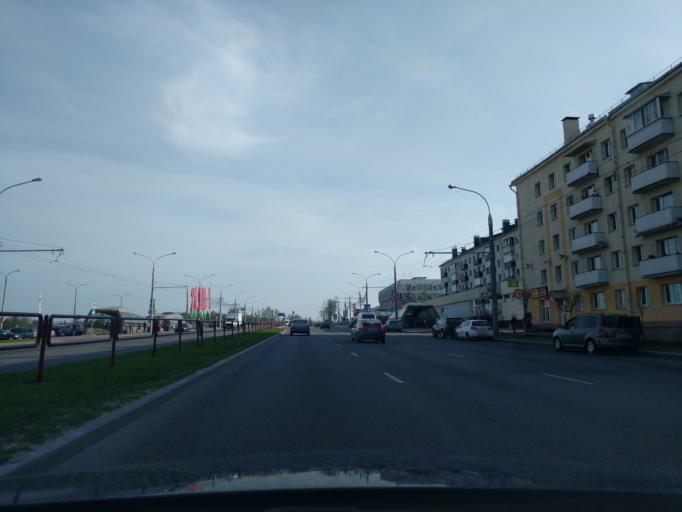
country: BY
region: Minsk
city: Minsk
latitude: 53.8611
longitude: 27.5718
